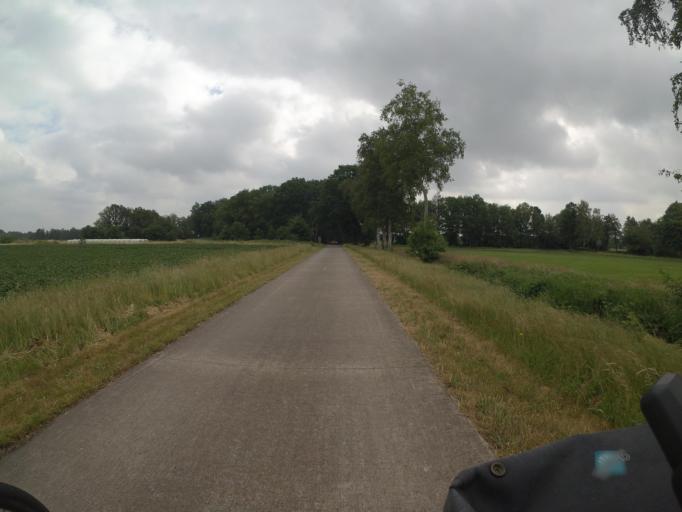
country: NL
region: Drenthe
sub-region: Gemeente Westerveld
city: Dwingeloo
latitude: 52.8391
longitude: 6.2885
